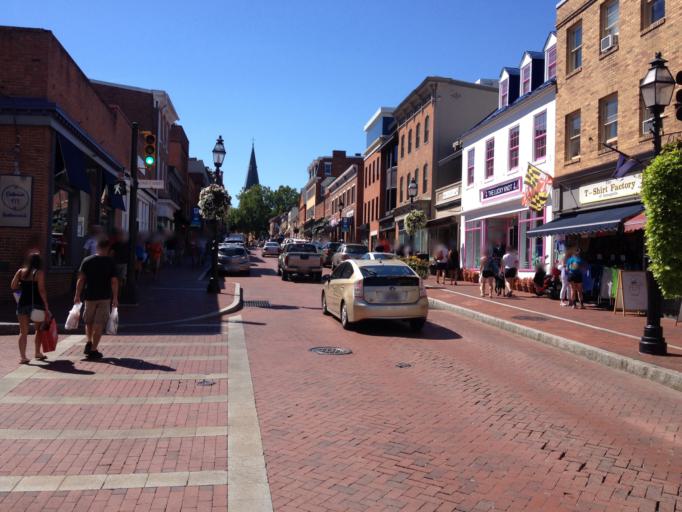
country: US
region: Maryland
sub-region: Anne Arundel County
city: Annapolis
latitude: 38.9778
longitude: -76.4900
